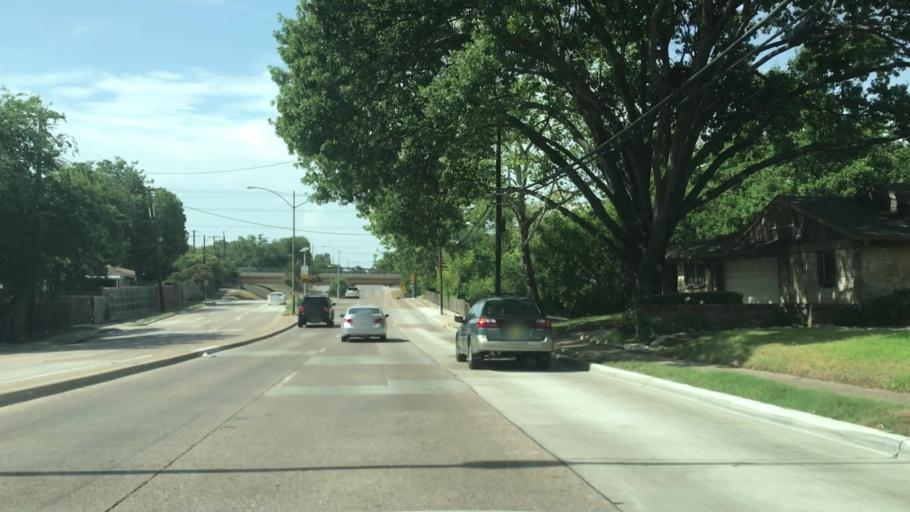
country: US
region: Texas
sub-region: Dallas County
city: Highland Park
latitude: 32.8419
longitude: -96.7529
